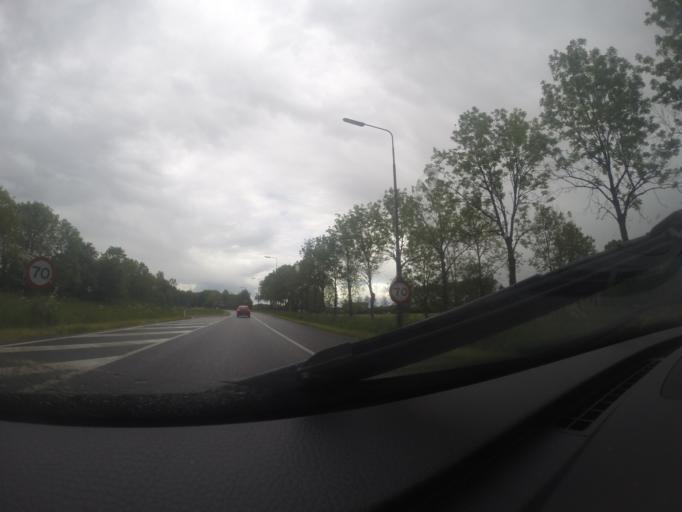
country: NL
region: Gelderland
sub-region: Gemeente Brummen
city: Brummen
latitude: 52.1048
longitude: 6.1685
